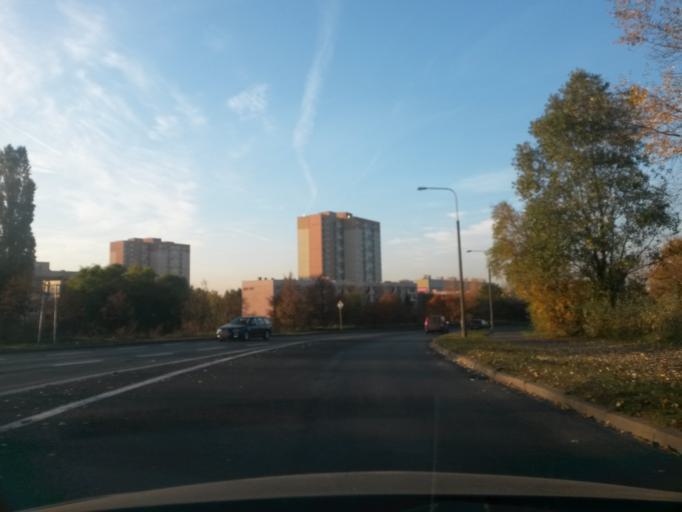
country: PL
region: Greater Poland Voivodeship
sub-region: Poznan
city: Poznan
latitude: 52.3783
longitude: 16.9569
